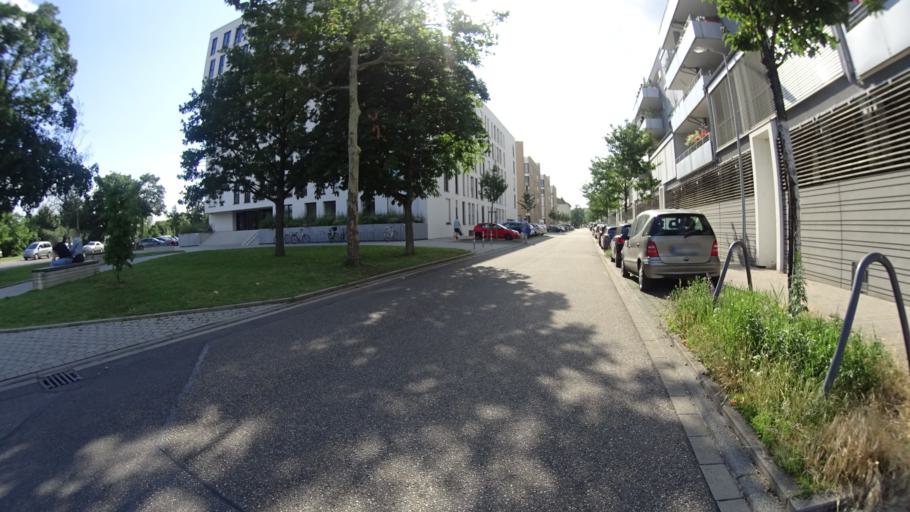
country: DE
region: Baden-Wuerttemberg
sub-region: Karlsruhe Region
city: Karlsruhe
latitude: 49.0003
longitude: 8.4196
